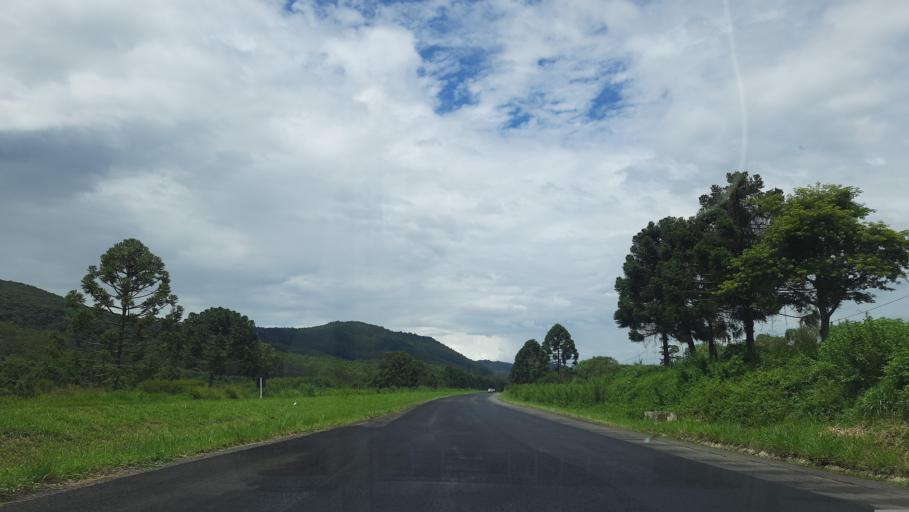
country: BR
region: Minas Gerais
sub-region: Pocos De Caldas
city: Pocos de Caldas
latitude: -21.8174
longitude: -46.6623
